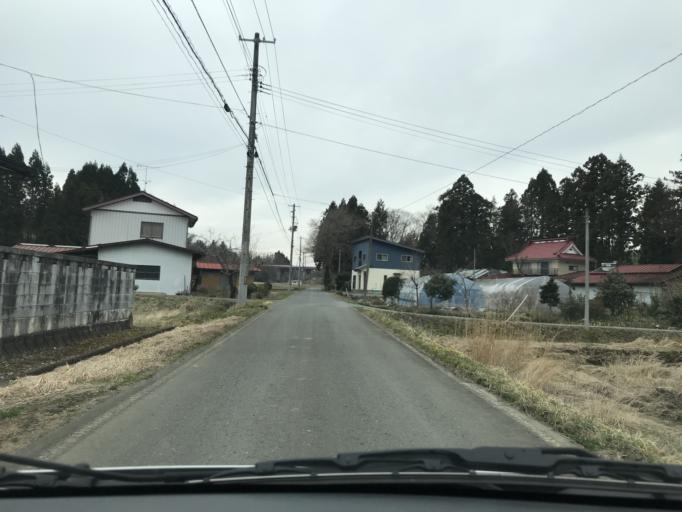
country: JP
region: Iwate
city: Mizusawa
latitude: 39.0922
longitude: 141.1186
